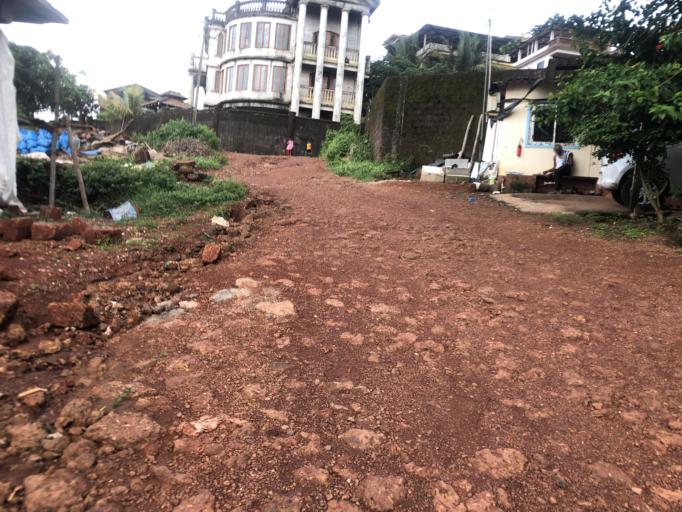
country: IN
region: Goa
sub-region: North Goa
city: Serula
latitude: 15.5502
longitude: 73.8260
